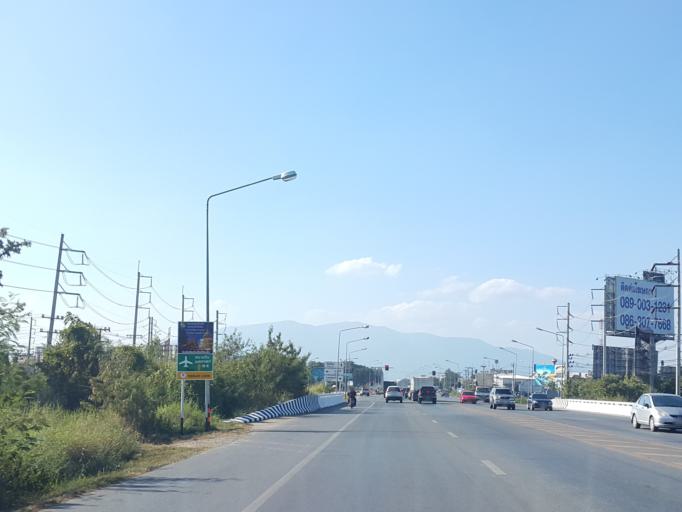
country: TH
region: Chiang Mai
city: Saraphi
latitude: 18.7519
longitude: 99.0603
